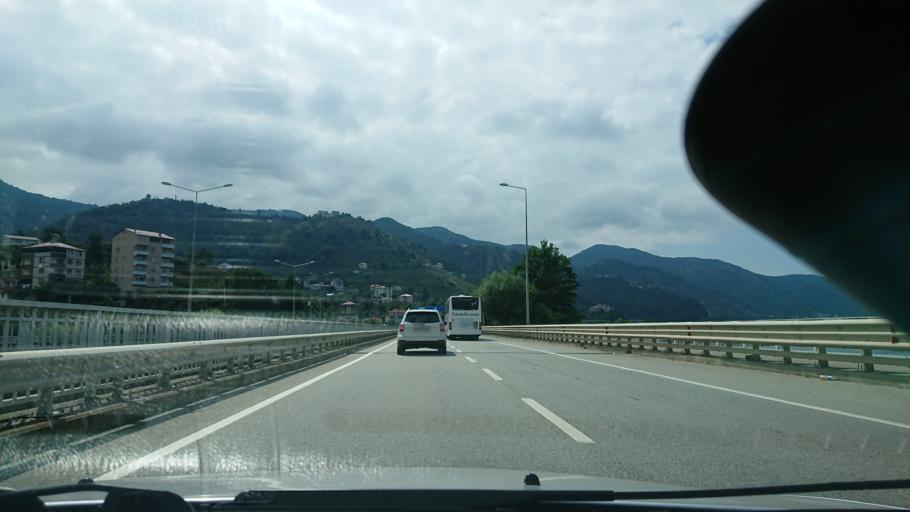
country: TR
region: Trabzon
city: Espiye
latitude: 40.9475
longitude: 38.6923
